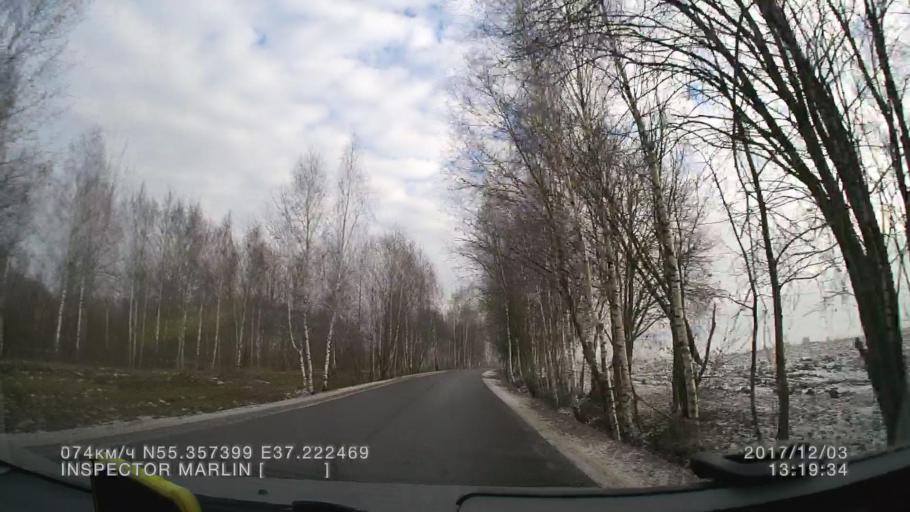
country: RU
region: Moskovskaya
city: Troitsk
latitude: 55.3574
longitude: 37.2226
